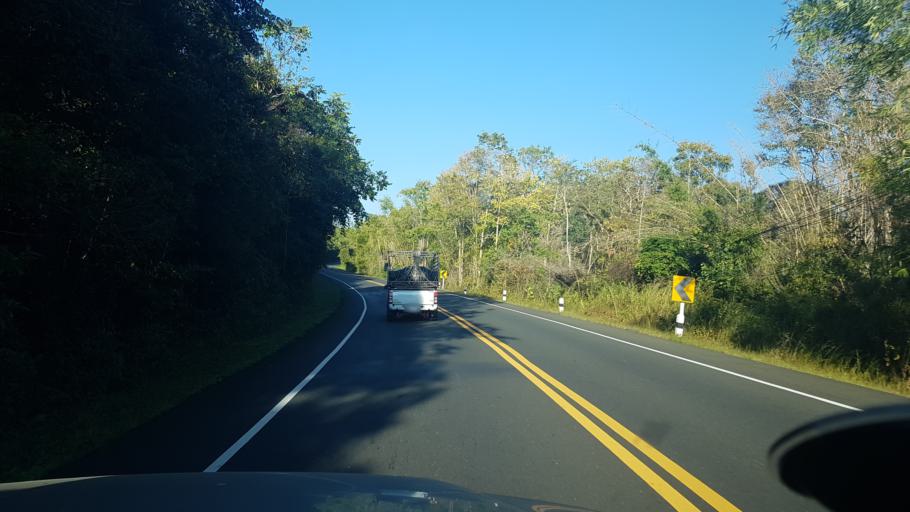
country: TH
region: Phetchabun
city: Nam Nao
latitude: 16.7012
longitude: 101.6168
